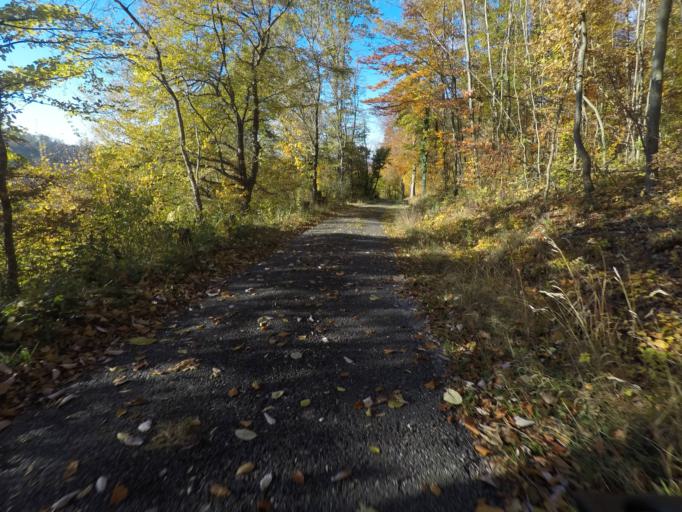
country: DE
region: Baden-Wuerttemberg
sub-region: Tuebingen Region
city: Pfullingen
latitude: 48.4405
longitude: 9.2167
